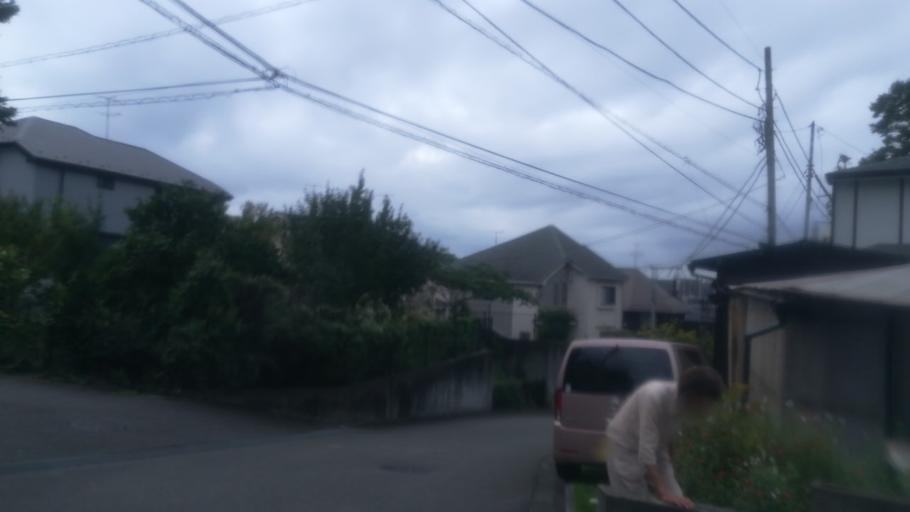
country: JP
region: Tokyo
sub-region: Machida-shi
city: Machida
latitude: 35.5872
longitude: 139.3976
